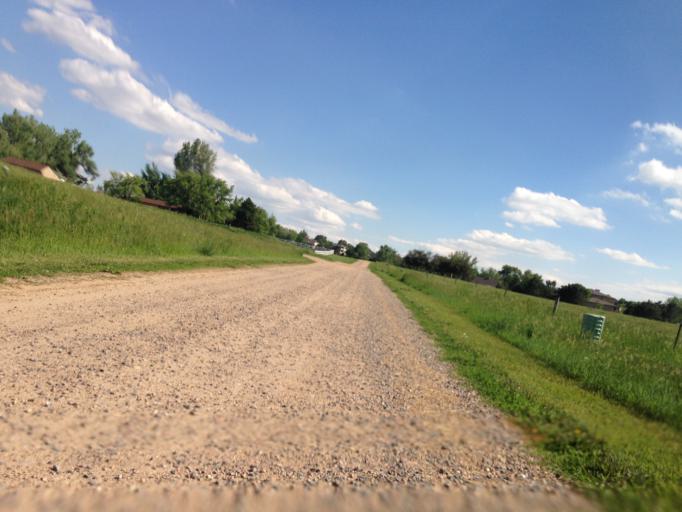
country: US
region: Colorado
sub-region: Boulder County
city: Lafayette
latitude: 40.0128
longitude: -105.1158
